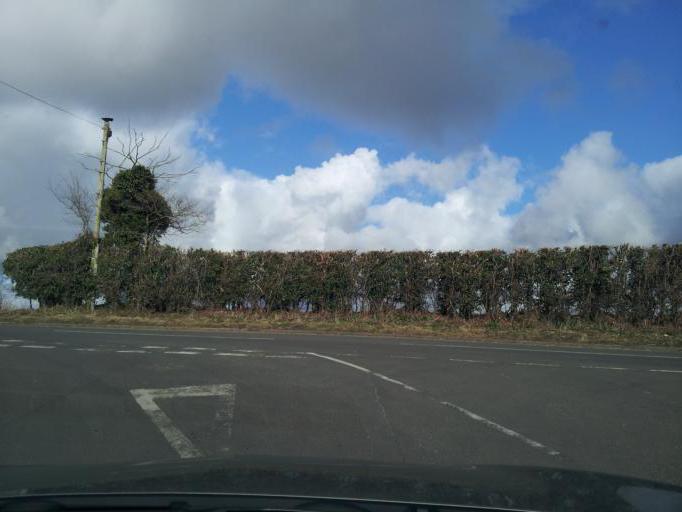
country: GB
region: England
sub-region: Norfolk
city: Costessey
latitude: 52.7047
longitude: 1.1550
